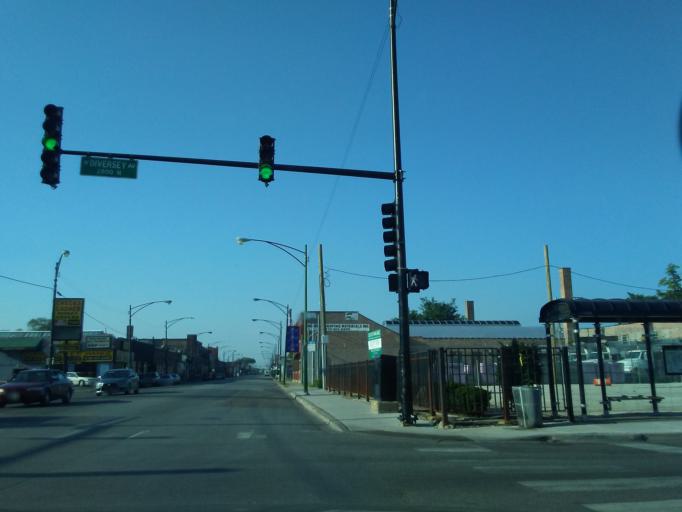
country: US
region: Illinois
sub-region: Cook County
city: Lincolnwood
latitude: 41.9318
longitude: -87.7271
